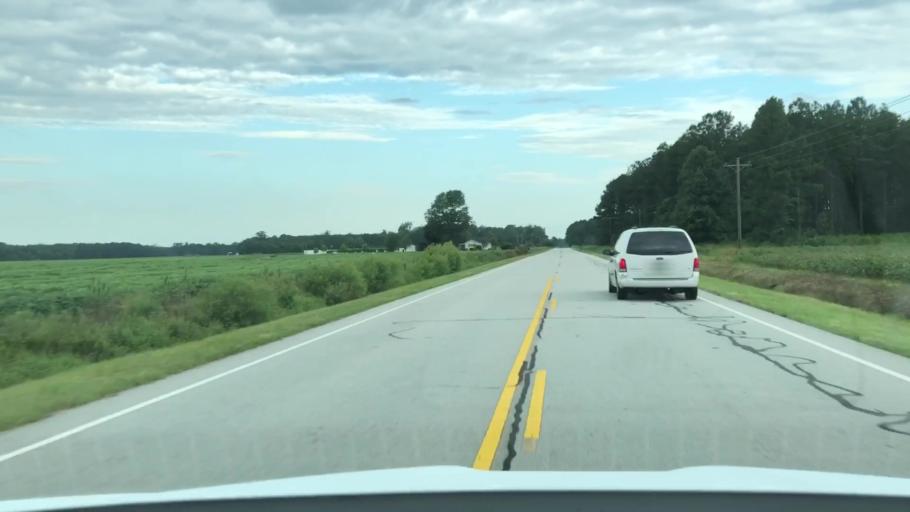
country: US
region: North Carolina
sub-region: Jones County
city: Trenton
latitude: 35.0801
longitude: -77.4320
